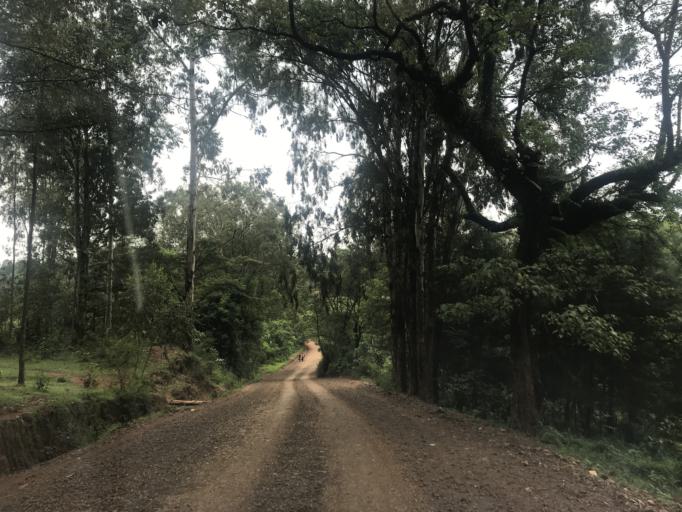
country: ET
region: Oromiya
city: Shambu
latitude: 9.8821
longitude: 36.6472
